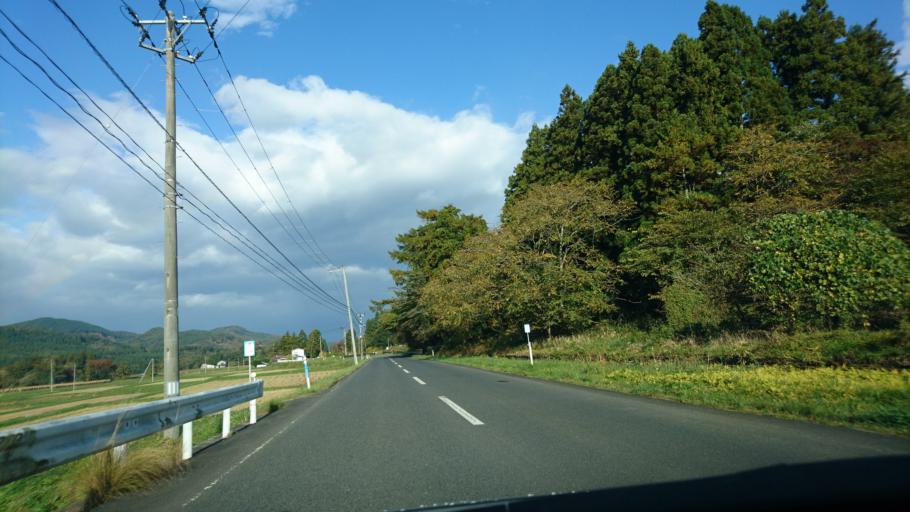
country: JP
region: Iwate
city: Mizusawa
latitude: 39.0468
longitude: 141.0531
